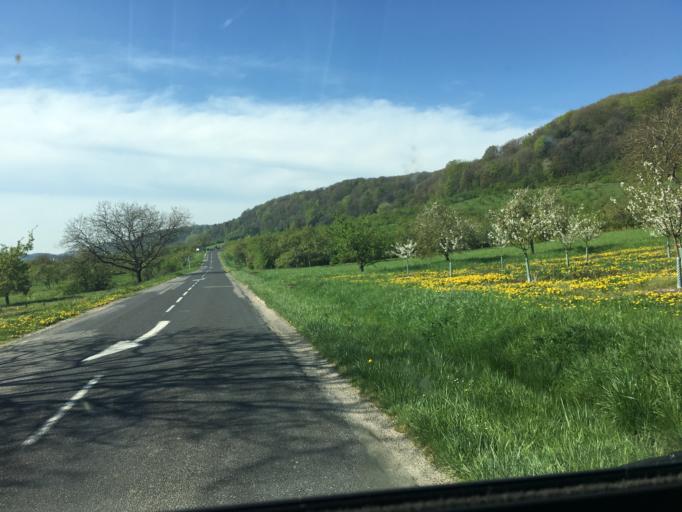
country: FR
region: Lorraine
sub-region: Departement de la Meuse
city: Vigneulles-les-Hattonchatel
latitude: 48.9118
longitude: 5.6685
